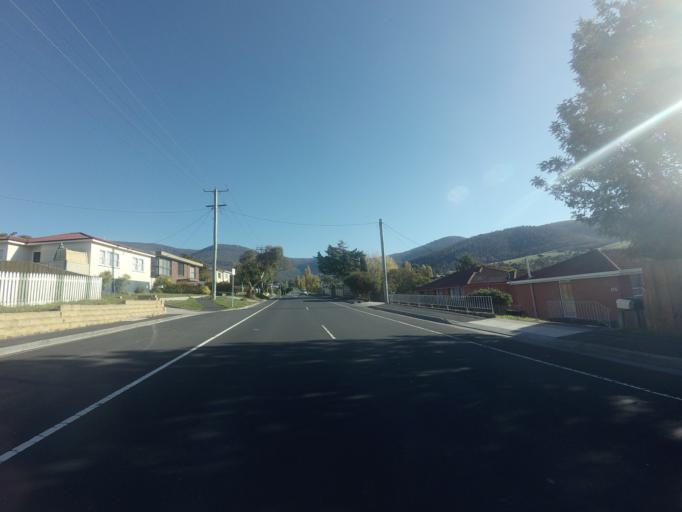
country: AU
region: Tasmania
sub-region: Glenorchy
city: Glenorchy
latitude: -42.8477
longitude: 147.2618
